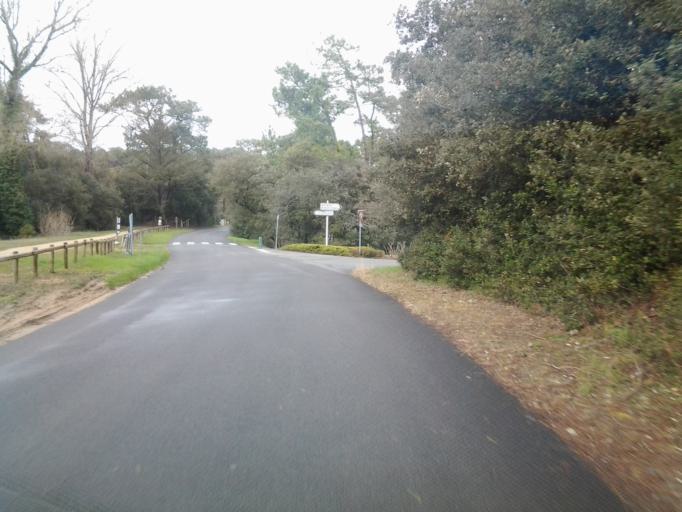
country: FR
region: Pays de la Loire
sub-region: Departement de la Vendee
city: La Tranche-sur-Mer
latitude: 46.3539
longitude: -1.4595
